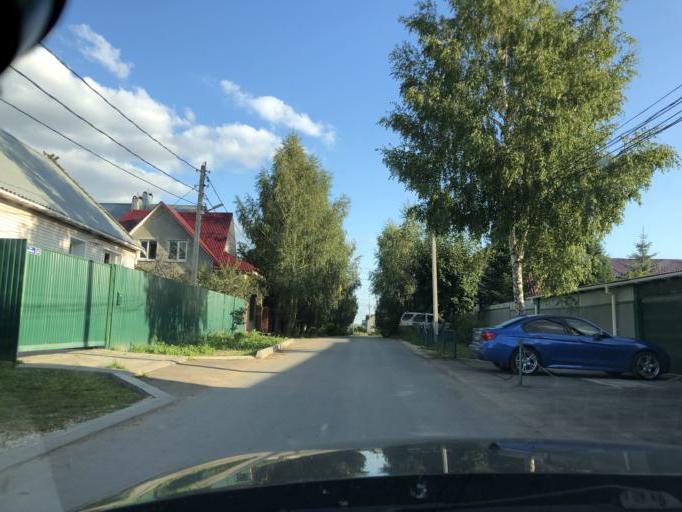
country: RU
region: Tula
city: Kosaya Gora
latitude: 54.1775
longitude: 37.5437
